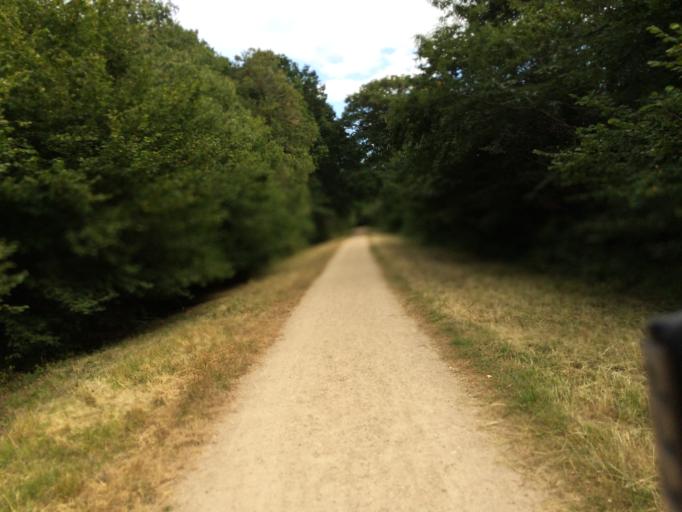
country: FR
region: Ile-de-France
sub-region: Departement de l'Essonne
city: Soisy-sur-Seine
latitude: 48.6714
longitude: 2.4473
